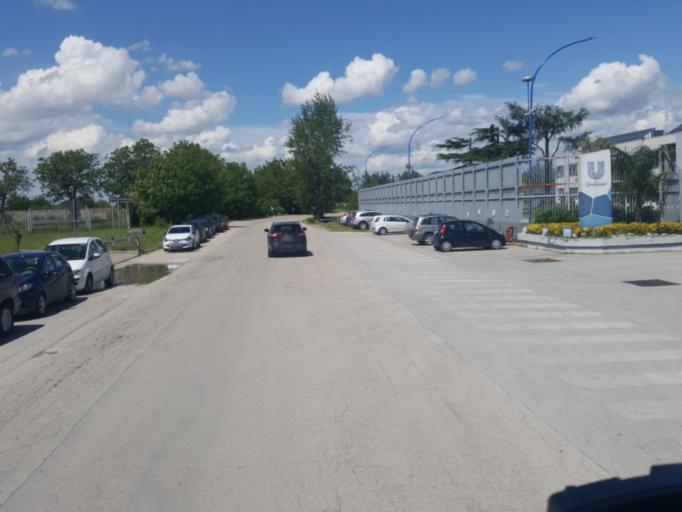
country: IT
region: Campania
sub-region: Provincia di Napoli
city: Pascarola
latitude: 40.9821
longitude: 14.2966
